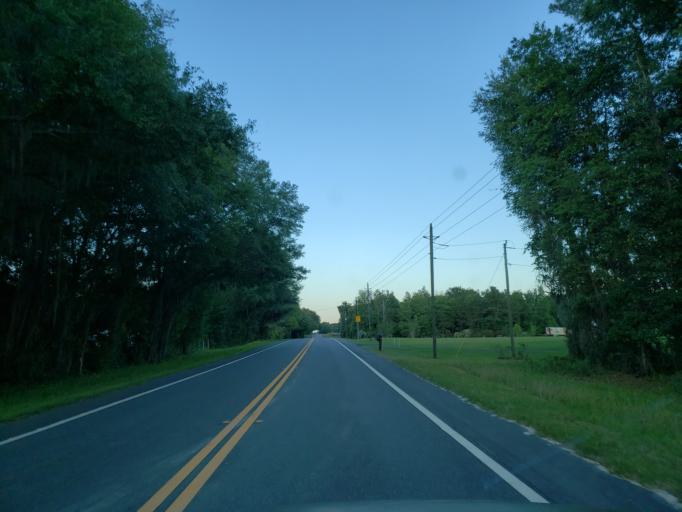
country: US
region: Georgia
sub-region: Echols County
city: Statenville
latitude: 30.5813
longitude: -83.2162
